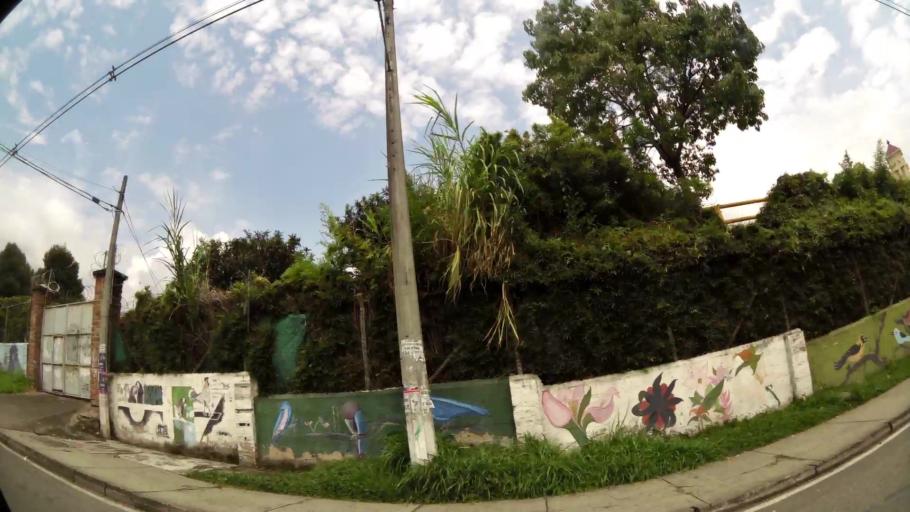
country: CO
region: Antioquia
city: Medellin
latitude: 6.2451
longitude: -75.6176
